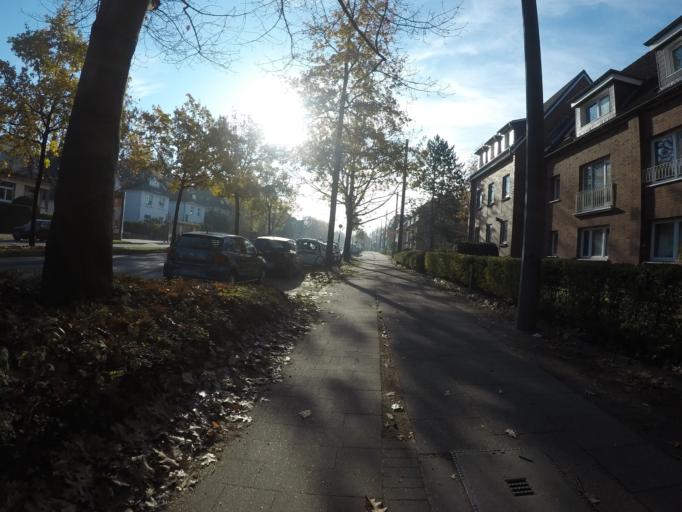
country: DE
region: Hamburg
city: Hamburg-Nord
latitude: 53.5950
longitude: 9.9662
